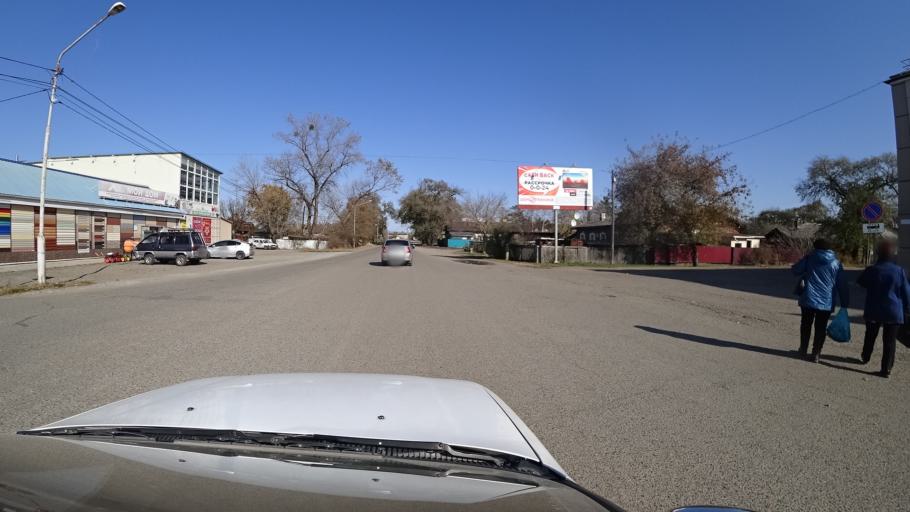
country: RU
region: Primorskiy
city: Dal'nerechensk
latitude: 45.9351
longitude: 133.7254
